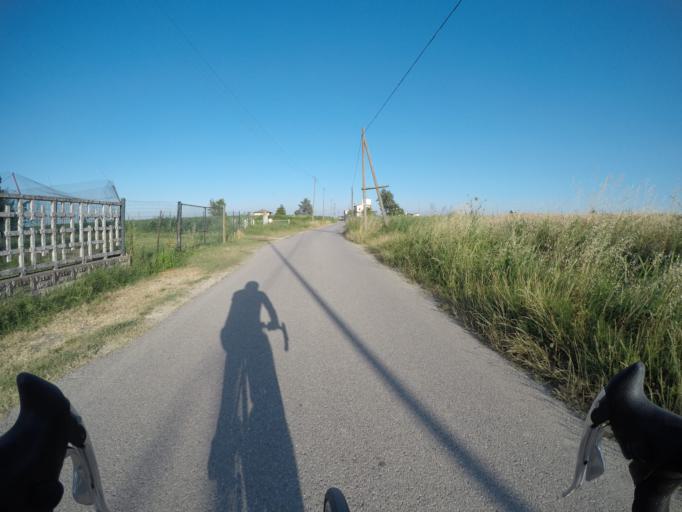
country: IT
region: Veneto
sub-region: Provincia di Rovigo
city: Fratta Polesine
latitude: 45.0283
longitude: 11.6550
